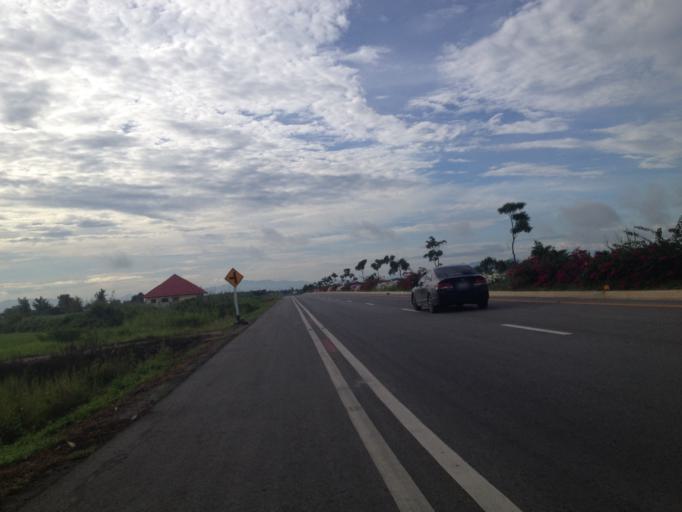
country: TH
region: Chiang Mai
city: San Pa Tong
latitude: 18.5787
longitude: 98.8438
